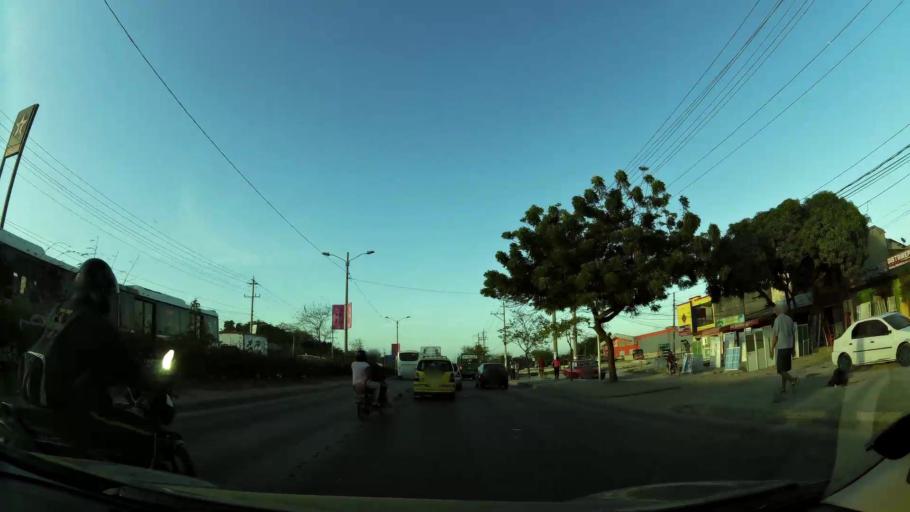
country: CO
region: Atlantico
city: Soledad
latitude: 10.9133
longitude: -74.7991
